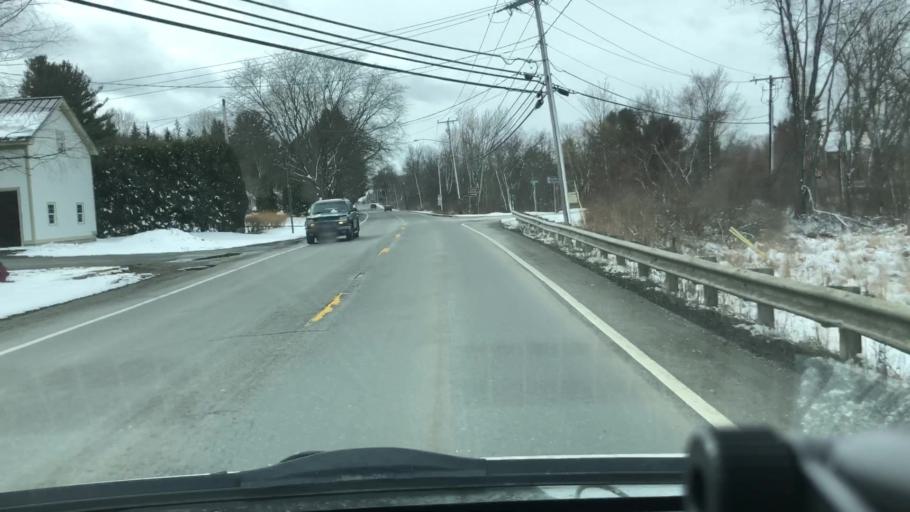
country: US
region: Massachusetts
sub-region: Franklin County
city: Greenfield
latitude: 42.5528
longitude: -72.5998
